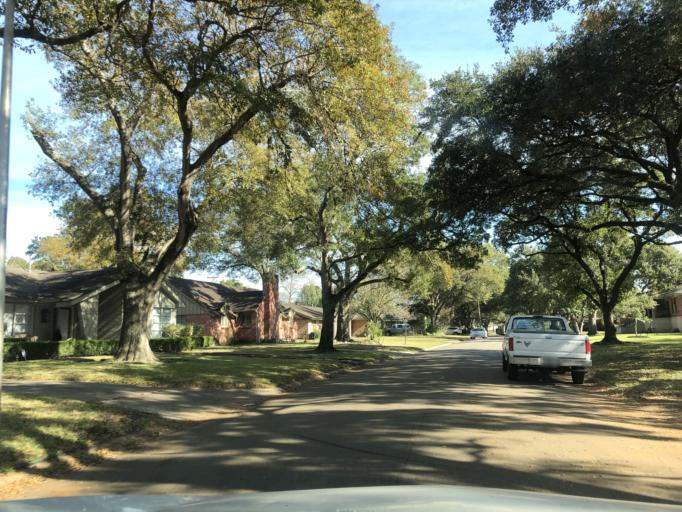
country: US
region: Texas
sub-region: Fort Bend County
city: Missouri City
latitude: 29.6785
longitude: -95.5171
